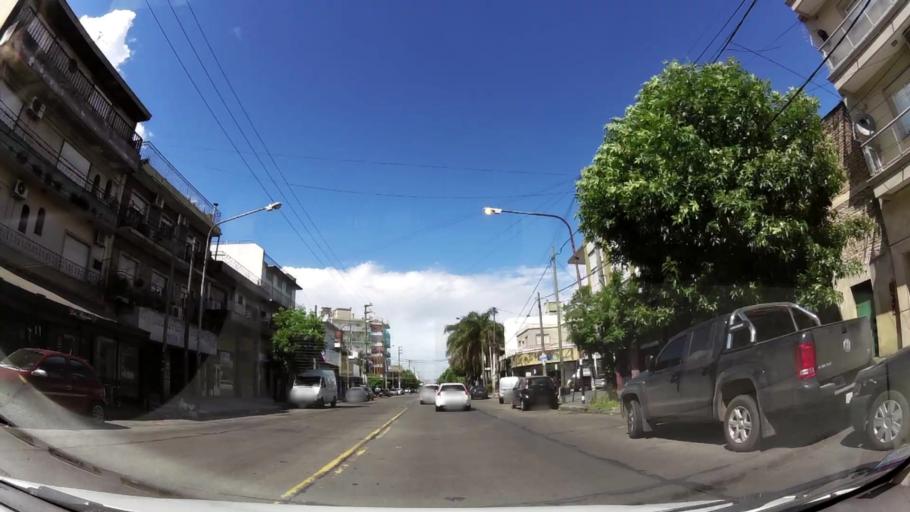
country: AR
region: Buenos Aires
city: San Justo
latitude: -34.6666
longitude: -58.5492
